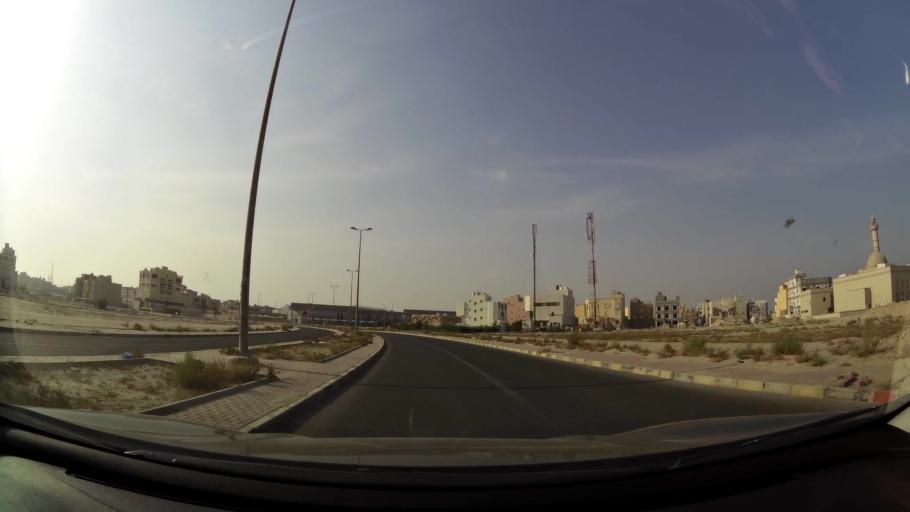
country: KW
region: Mubarak al Kabir
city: Mubarak al Kabir
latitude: 29.1939
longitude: 48.1047
